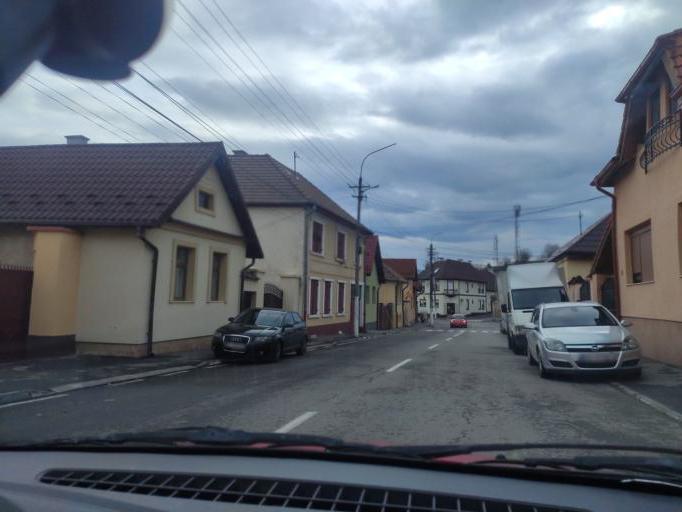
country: RO
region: Brasov
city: Codlea
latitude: 45.6975
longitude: 25.4396
